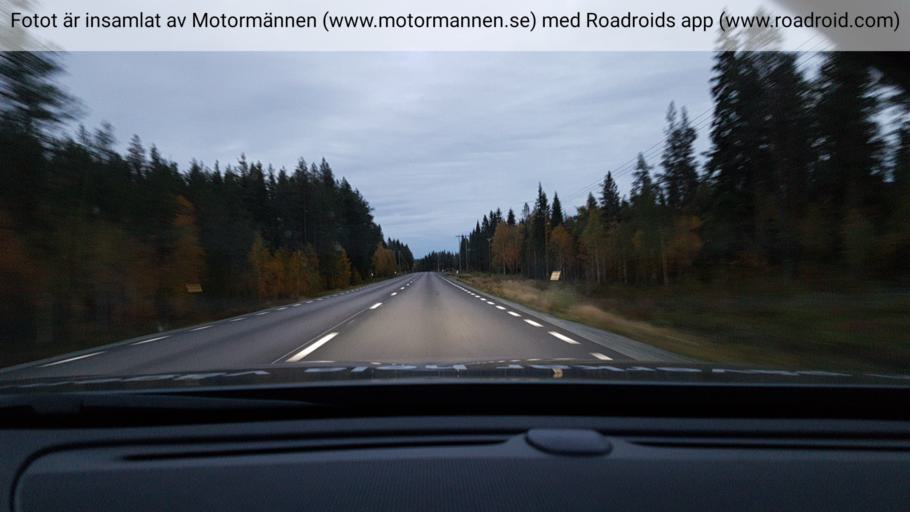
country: SE
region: Norrbotten
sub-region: Alvsbyns Kommun
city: AElvsbyn
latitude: 65.7506
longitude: 20.9099
